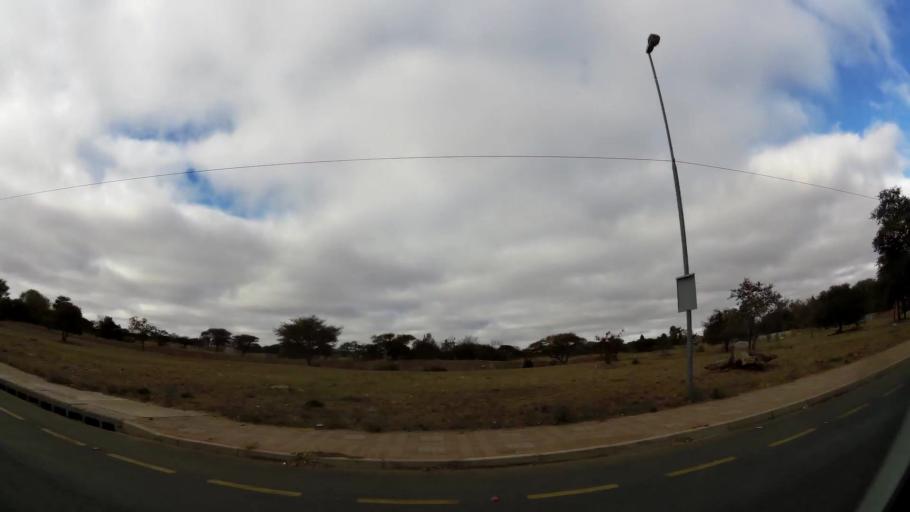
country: ZA
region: Limpopo
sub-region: Capricorn District Municipality
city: Polokwane
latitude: -23.9166
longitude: 29.4735
